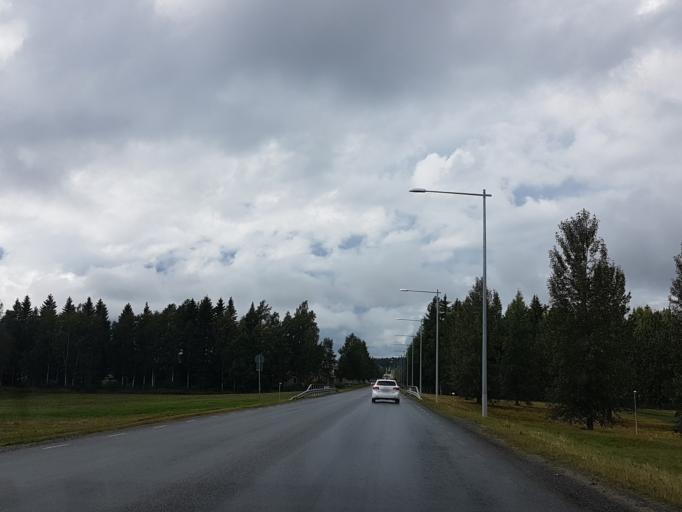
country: SE
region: Vaesterbotten
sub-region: Umea Kommun
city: Ersmark
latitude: 63.8518
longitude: 20.3229
